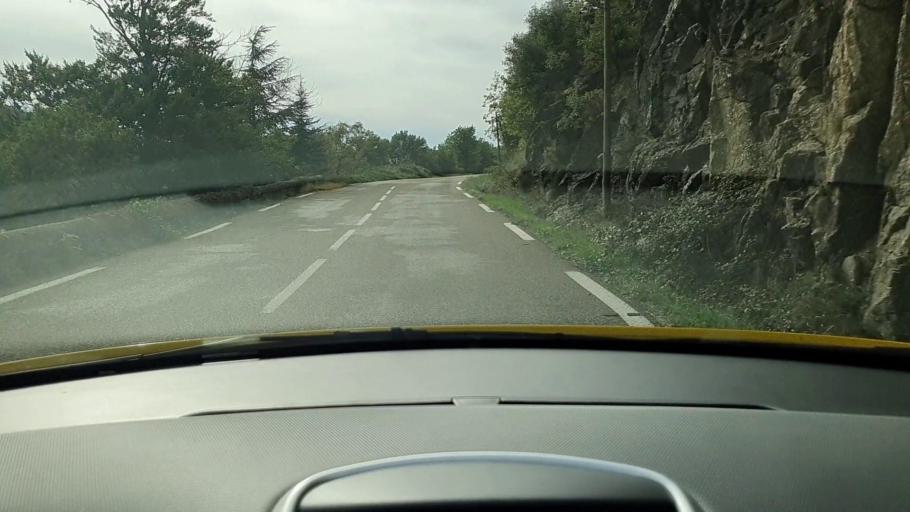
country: FR
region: Languedoc-Roussillon
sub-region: Departement du Gard
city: Le Vigan
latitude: 44.0422
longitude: 3.5888
